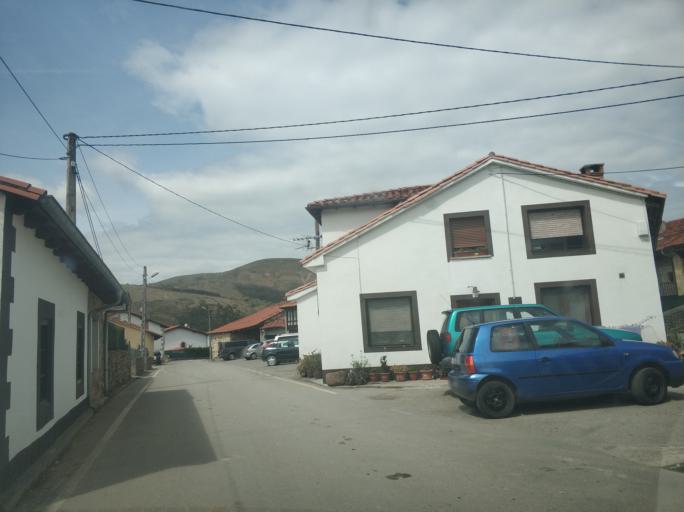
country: ES
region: Cantabria
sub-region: Provincia de Cantabria
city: Ruente
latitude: 43.2337
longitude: -4.2812
